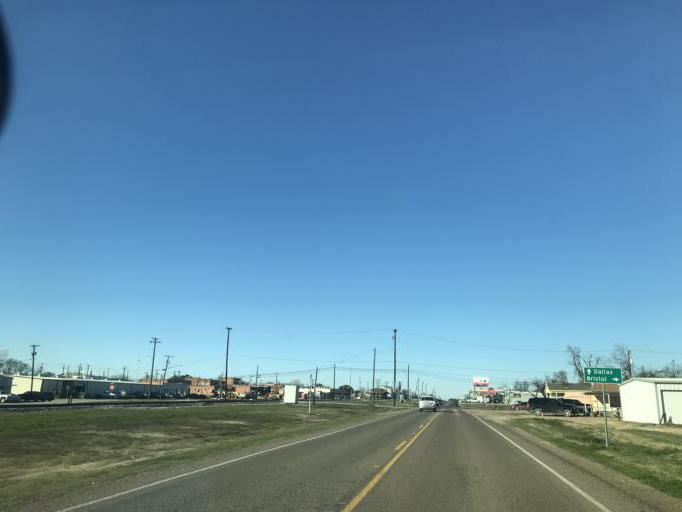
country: US
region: Texas
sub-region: Ellis County
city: Ferris
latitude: 32.5311
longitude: -96.6648
